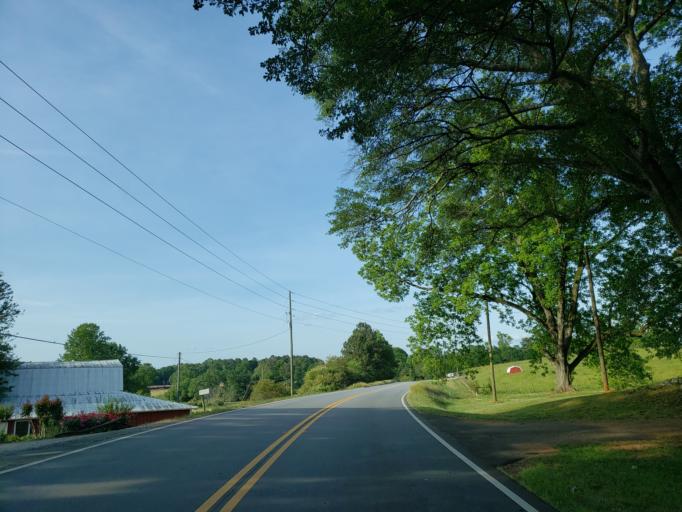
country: US
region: Georgia
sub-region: Carroll County
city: Bowdon
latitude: 33.4778
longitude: -85.2896
